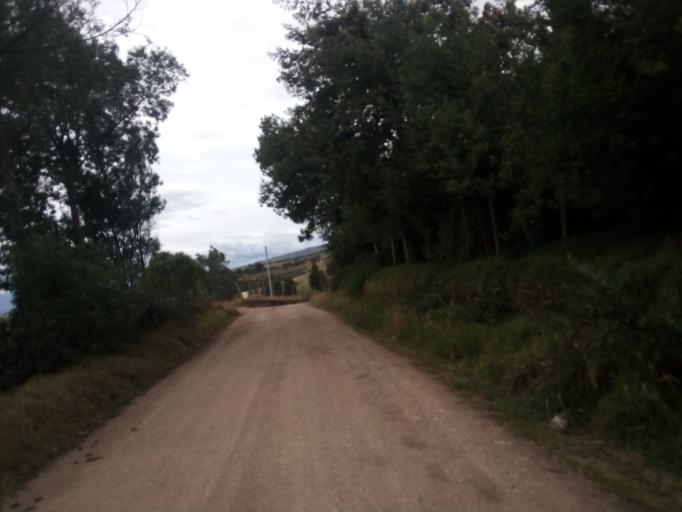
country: CO
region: Boyaca
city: Toca
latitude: 5.5759
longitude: -73.1513
